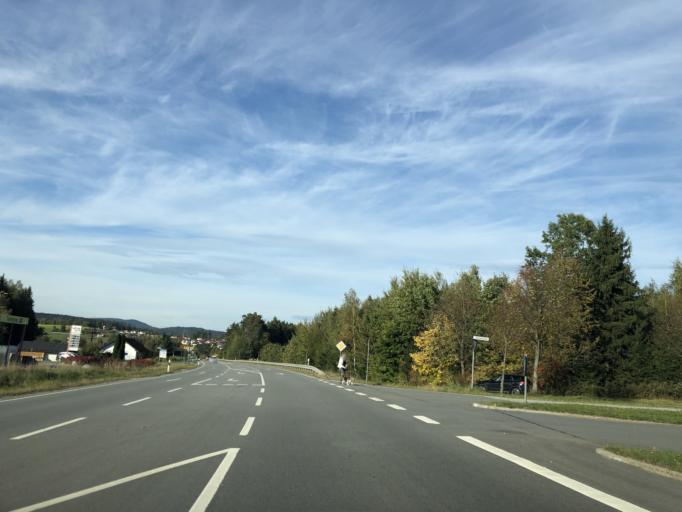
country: DE
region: Bavaria
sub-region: Lower Bavaria
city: Patersdorf
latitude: 49.0063
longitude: 12.9831
